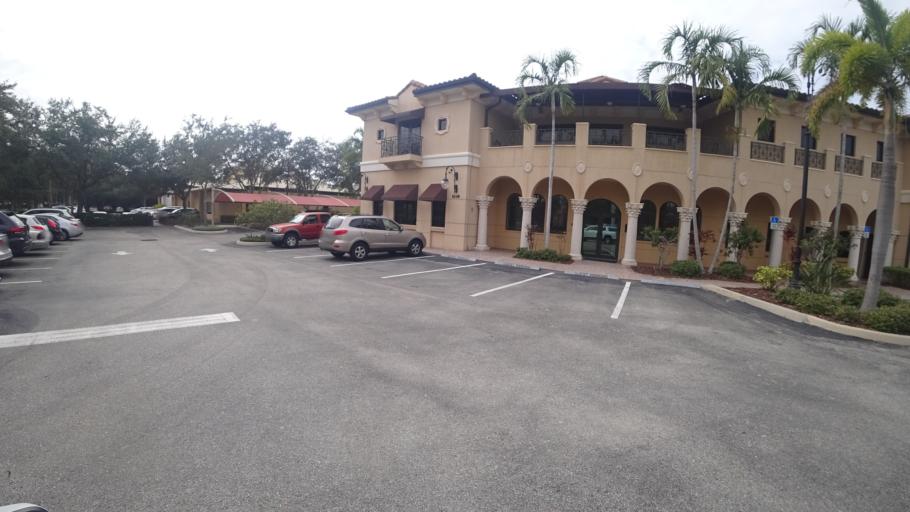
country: US
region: Florida
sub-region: Sarasota County
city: The Meadows
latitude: 27.3872
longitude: -82.4461
